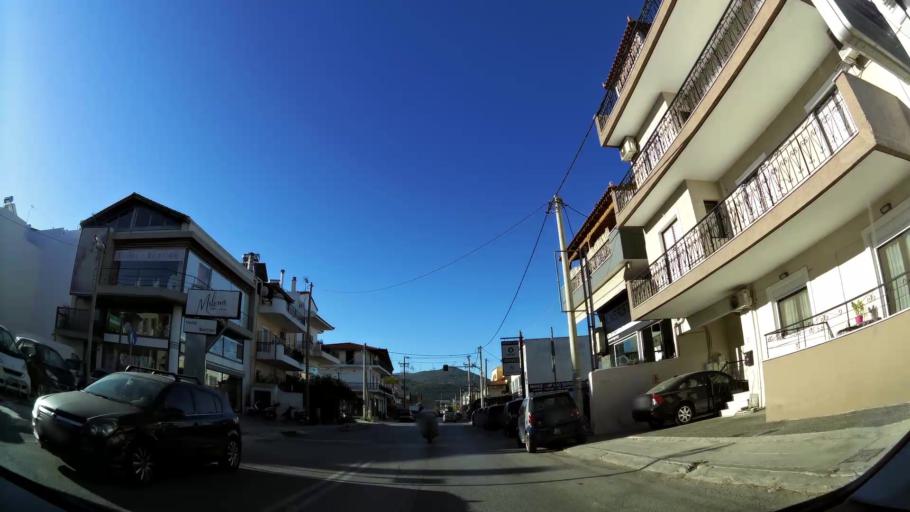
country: GR
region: Attica
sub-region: Nomarchia Anatolikis Attikis
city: Gerakas
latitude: 38.0187
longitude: 23.8458
